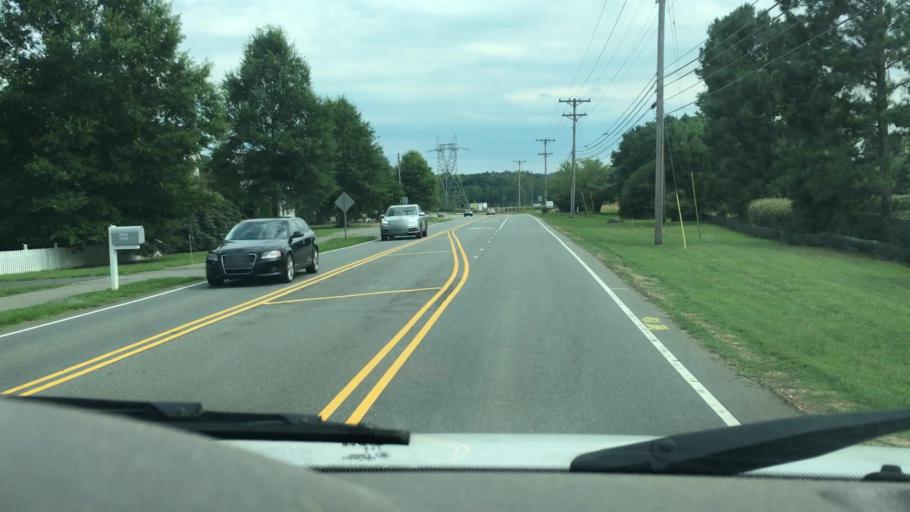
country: US
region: North Carolina
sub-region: Gaston County
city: Davidson
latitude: 35.4807
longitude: -80.8201
